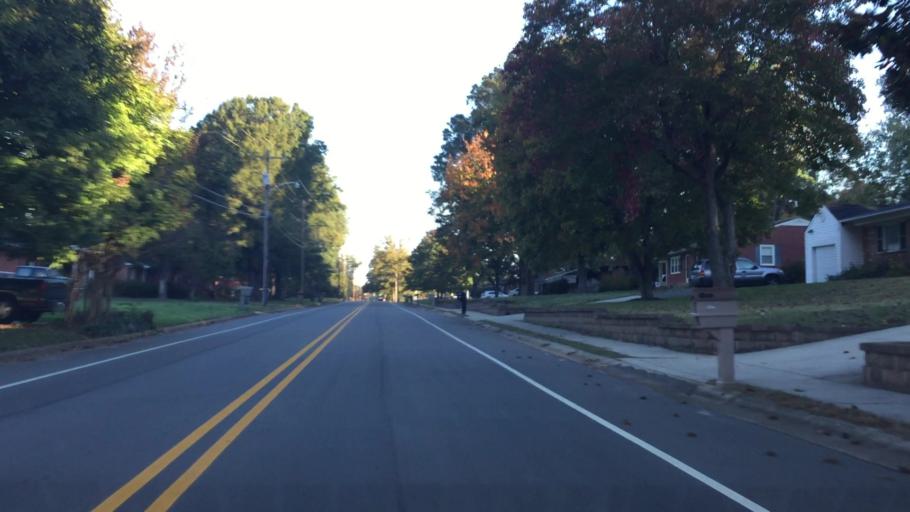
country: US
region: North Carolina
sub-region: Iredell County
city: Mooresville
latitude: 35.5722
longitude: -80.8014
